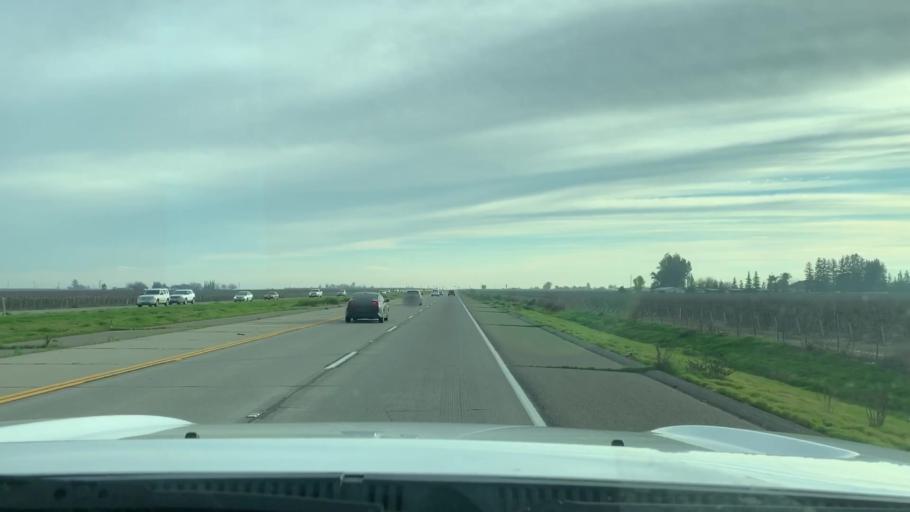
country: US
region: California
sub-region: Fresno County
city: Caruthers
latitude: 36.5590
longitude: -119.7863
